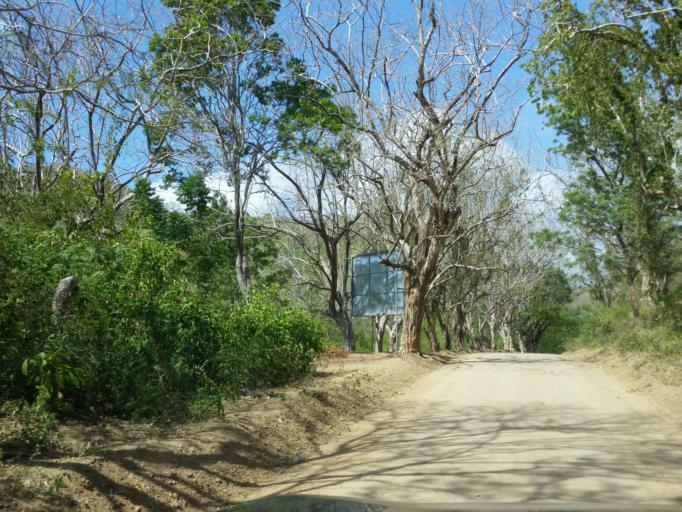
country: CR
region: Guanacaste
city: La Cruz
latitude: 11.1151
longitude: -85.7629
